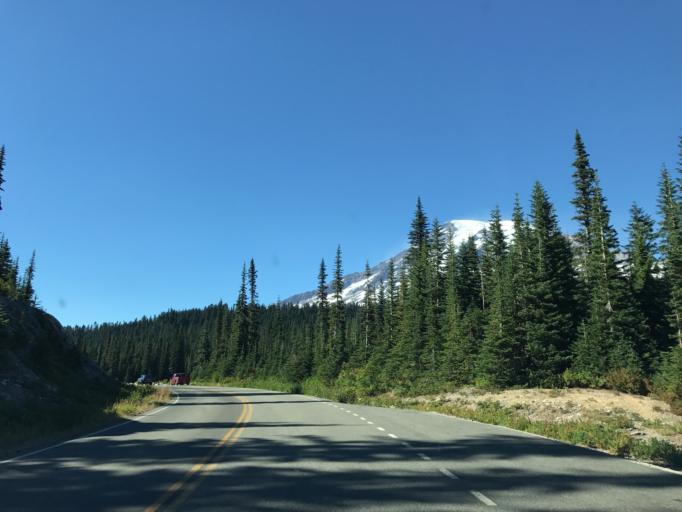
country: US
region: Washington
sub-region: Pierce County
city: Buckley
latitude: 46.7682
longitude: -121.7232
